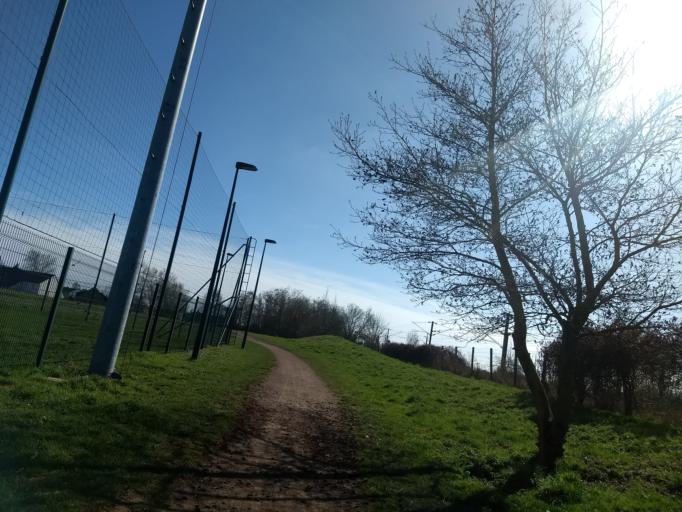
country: FR
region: Nord-Pas-de-Calais
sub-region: Departement du Pas-de-Calais
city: Achicourt
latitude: 50.2692
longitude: 2.7642
